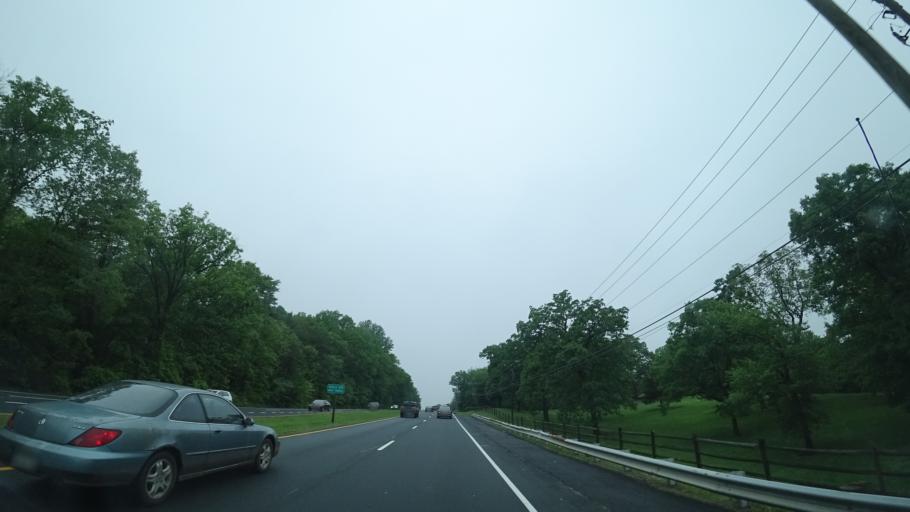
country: US
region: Virginia
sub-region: Fairfax County
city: Reston
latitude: 38.9745
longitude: -77.3242
